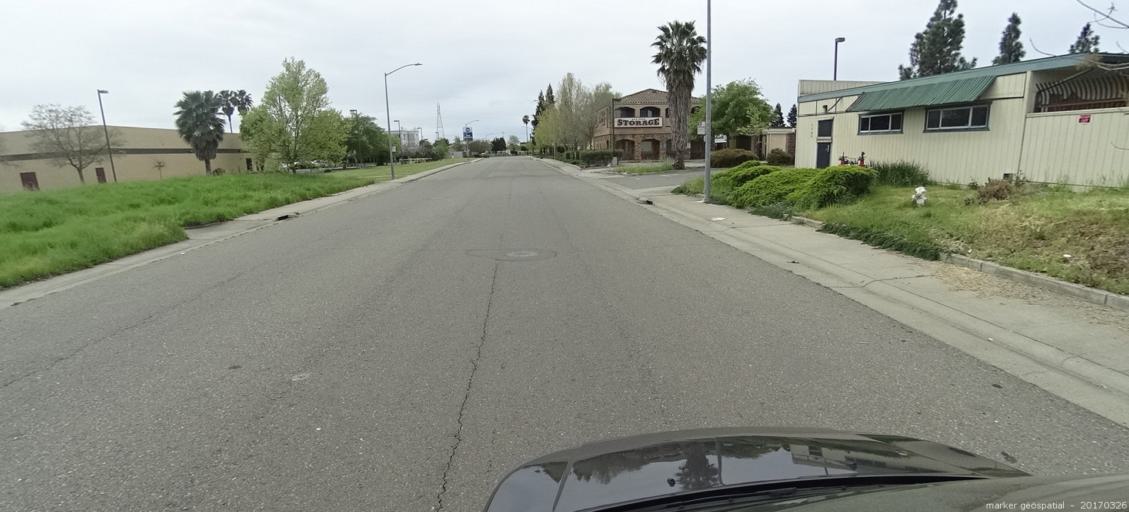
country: US
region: California
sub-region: Sacramento County
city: Florin
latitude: 38.4779
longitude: -121.4222
